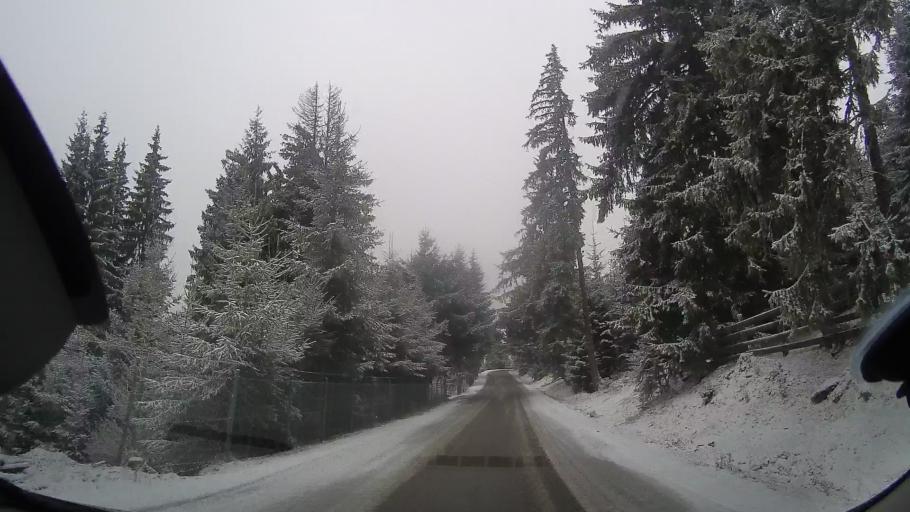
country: RO
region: Cluj
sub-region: Comuna Maguri-Racatau
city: Maguri
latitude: 46.6442
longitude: 23.0717
